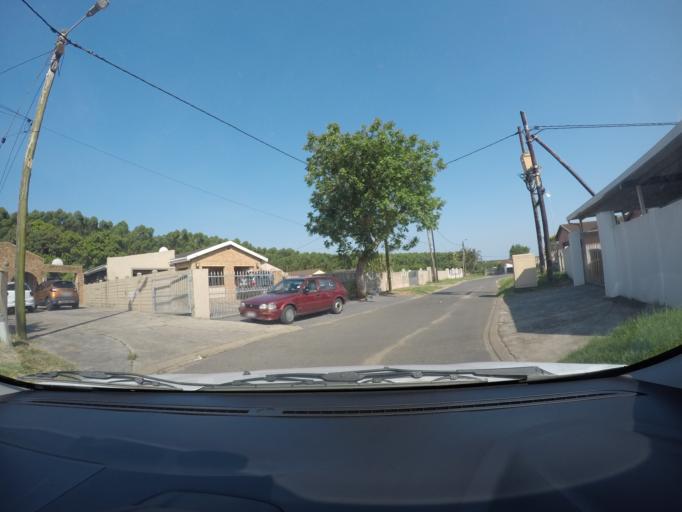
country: ZA
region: KwaZulu-Natal
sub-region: uThungulu District Municipality
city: Richards Bay
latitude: -28.7146
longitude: 32.0431
